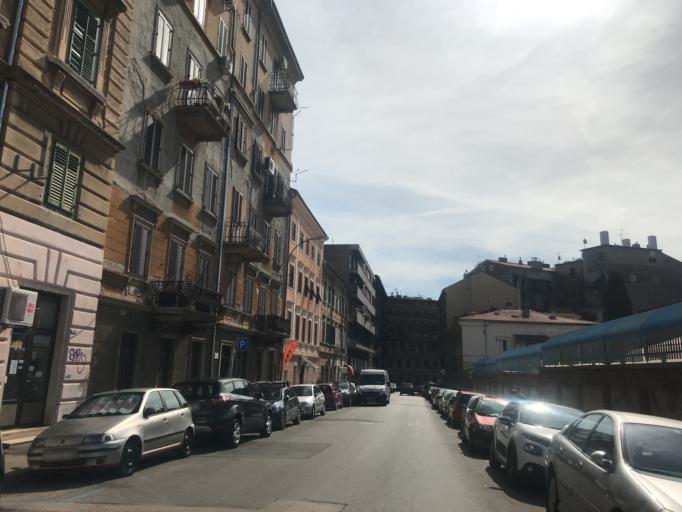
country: HR
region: Primorsko-Goranska
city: Drenova
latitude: 45.3312
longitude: 14.4360
